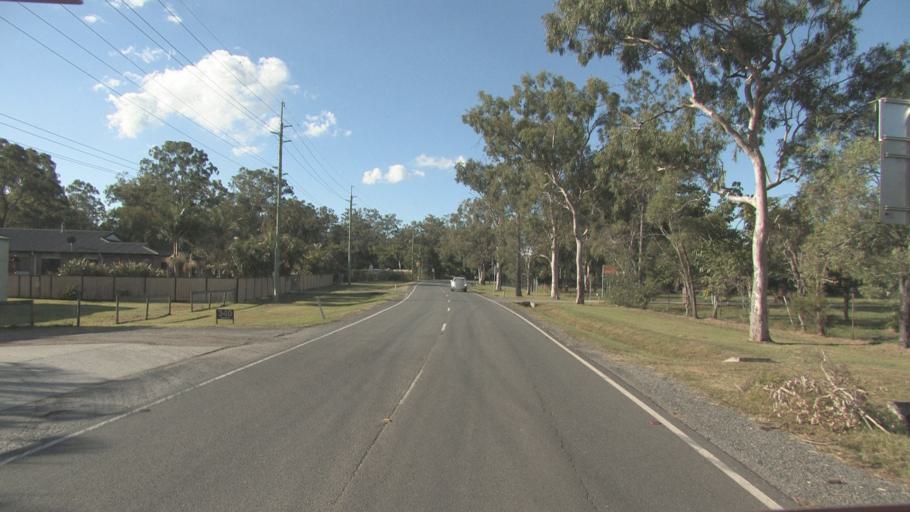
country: AU
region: Queensland
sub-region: Logan
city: Beenleigh
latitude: -27.6617
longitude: 153.2164
